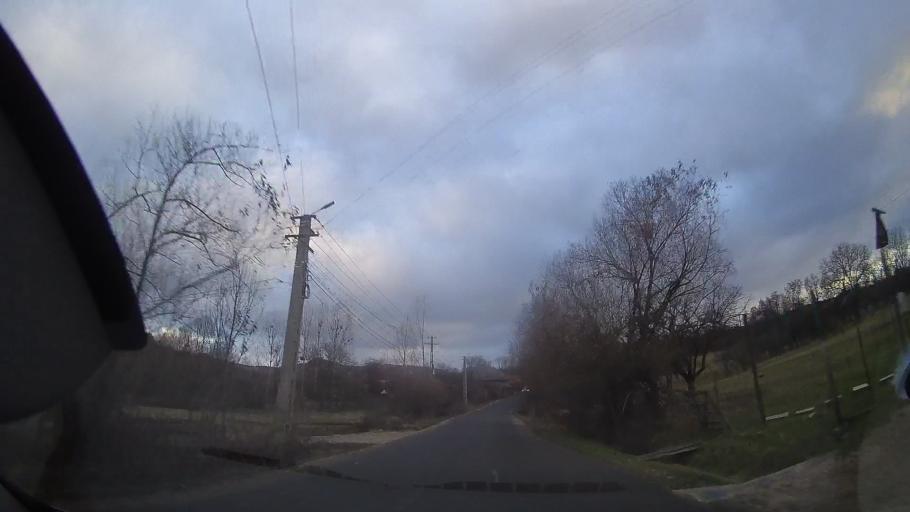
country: RO
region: Cluj
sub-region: Comuna Calatele
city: Calatele
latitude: 46.7830
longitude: 23.0212
